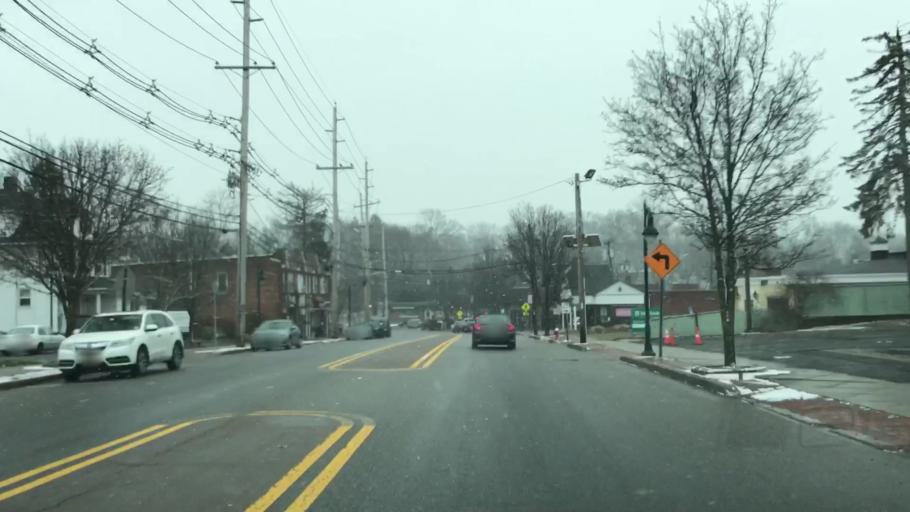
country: US
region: New Jersey
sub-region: Bergen County
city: Oradell
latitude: 40.9494
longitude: -74.0322
